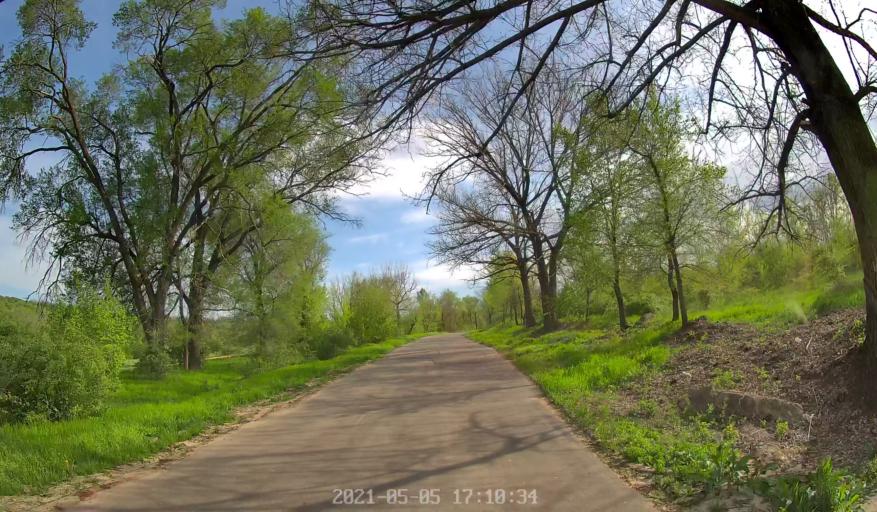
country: MD
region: Chisinau
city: Vadul lui Voda
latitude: 46.9998
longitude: 29.1113
